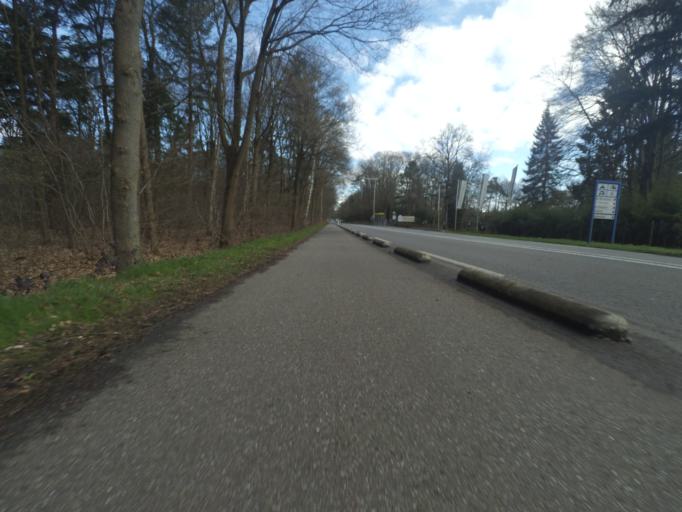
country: NL
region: Gelderland
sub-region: Gemeente Apeldoorn
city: Beekbergen
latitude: 52.1425
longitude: 5.9603
